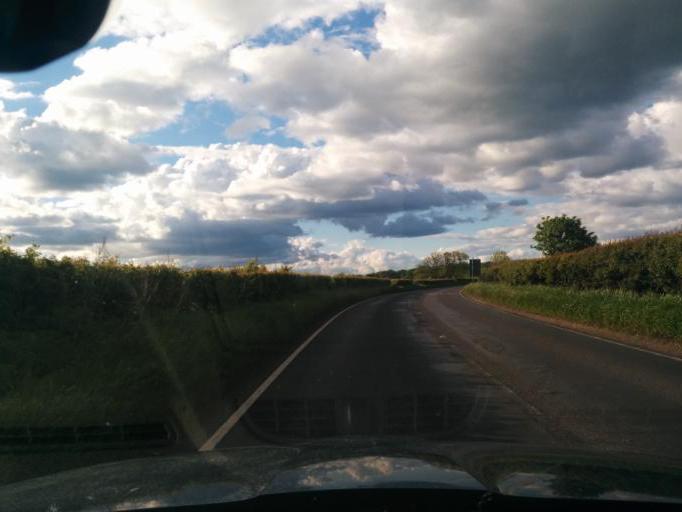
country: GB
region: England
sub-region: Northumberland
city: Bedlington
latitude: 55.1074
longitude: -1.6187
